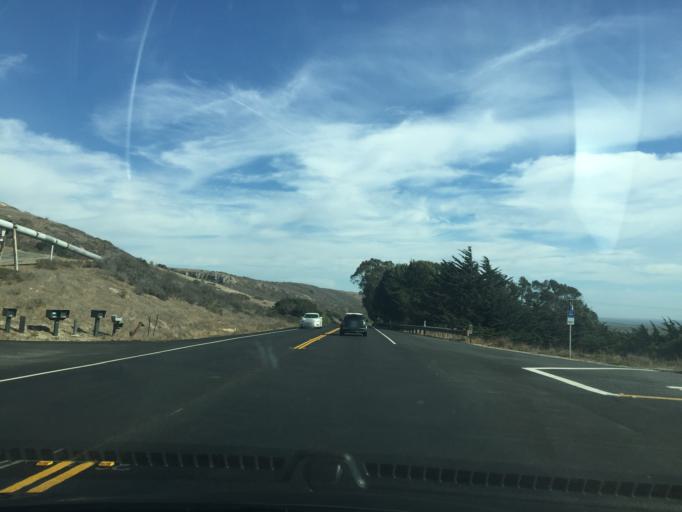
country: US
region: California
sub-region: Santa Cruz County
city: Bonny Doon
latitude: 36.9828
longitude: -122.1438
